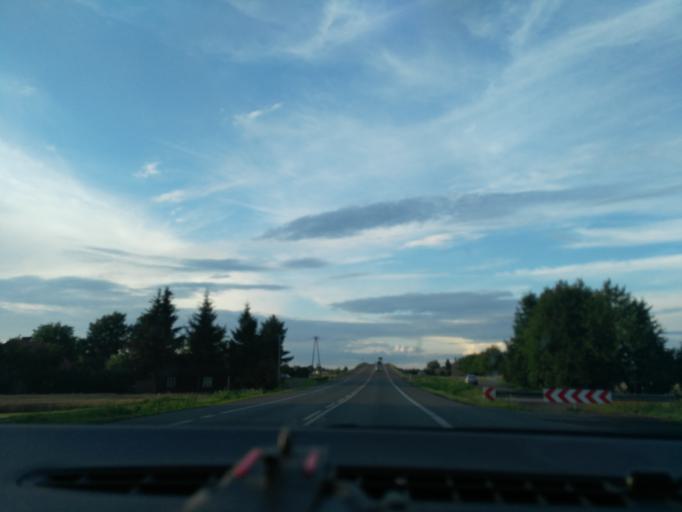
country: PL
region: Lublin Voivodeship
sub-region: Powiat lubelski
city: Niedrzwica Duza
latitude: 51.1238
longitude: 22.3916
